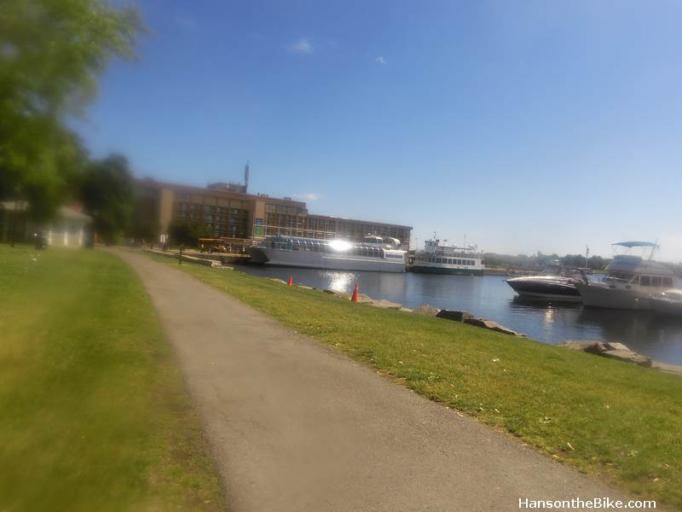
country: CA
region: Ontario
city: Kingston
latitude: 44.2295
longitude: -76.4793
